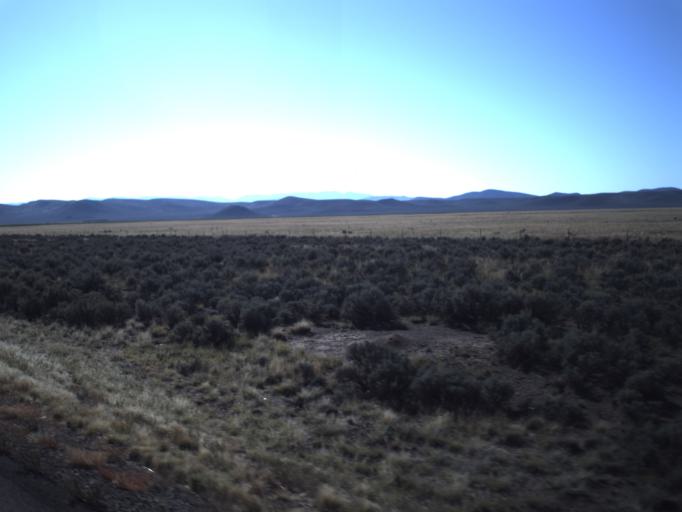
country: US
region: Utah
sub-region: Washington County
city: Enterprise
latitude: 37.7662
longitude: -113.8168
